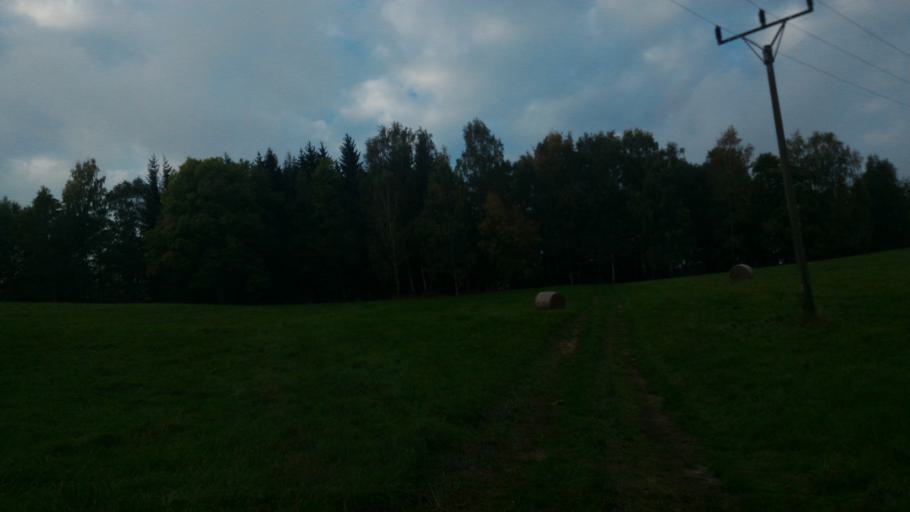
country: CZ
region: Ustecky
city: Dolni Podluzi
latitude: 50.8624
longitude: 14.5781
